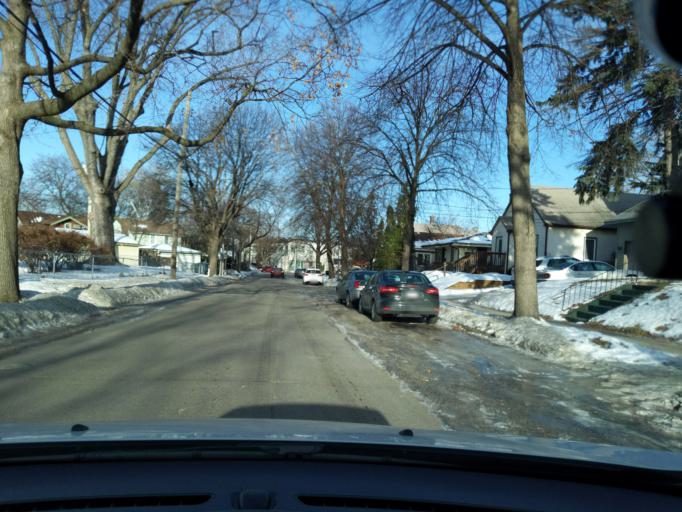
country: US
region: Minnesota
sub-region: Ramsey County
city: Lauderdale
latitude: 44.9868
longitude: -93.2203
